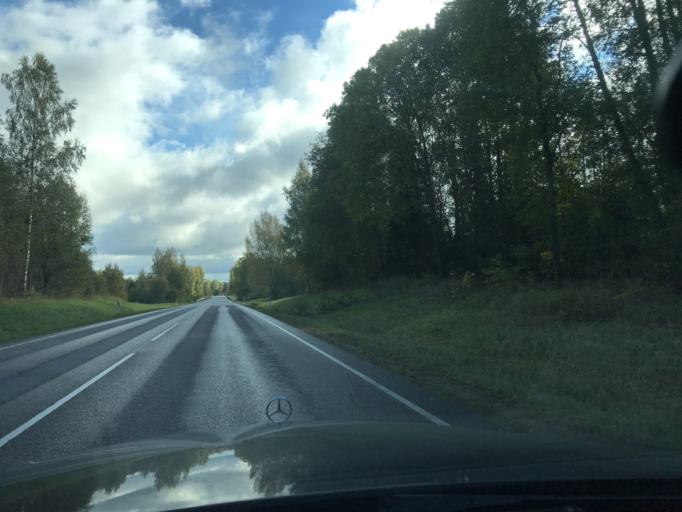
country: EE
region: Vorumaa
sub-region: Voru linn
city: Voru
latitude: 57.7725
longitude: 27.1444
